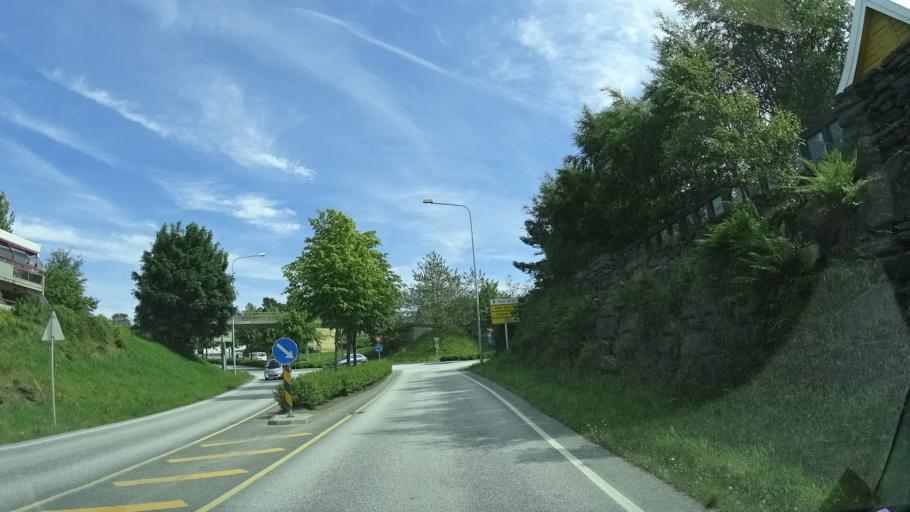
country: NO
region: Rogaland
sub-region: Stavanger
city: Stavanger
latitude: 58.9798
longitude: 5.6900
